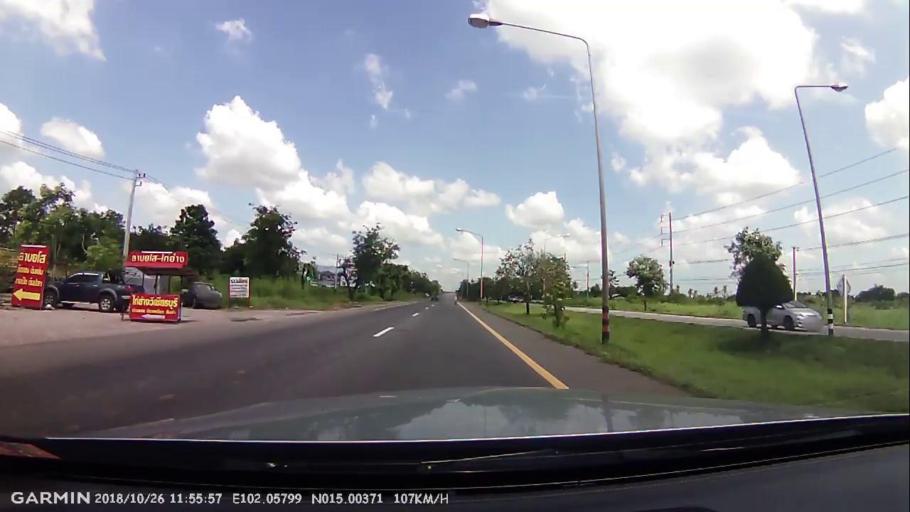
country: TH
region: Nakhon Ratchasima
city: Nakhon Ratchasima
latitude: 15.0038
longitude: 102.0581
